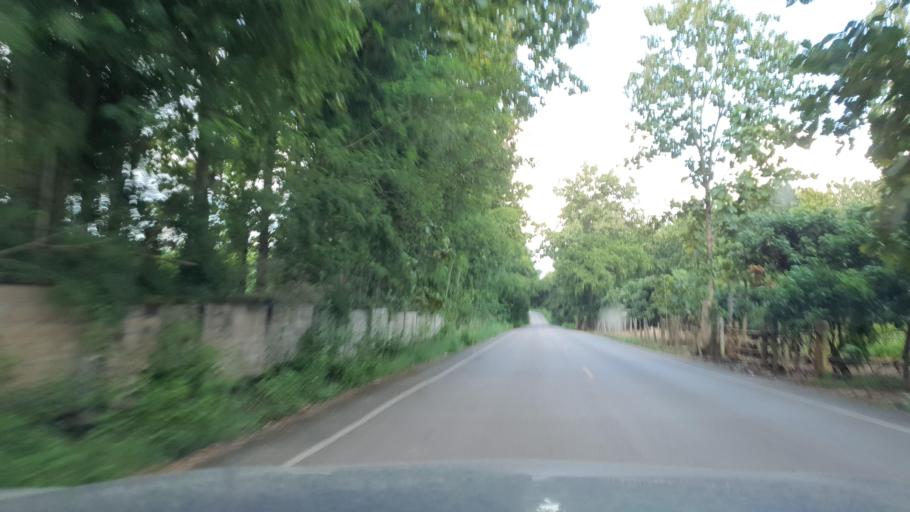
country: TH
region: Phayao
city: Phayao
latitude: 19.0945
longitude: 99.8296
